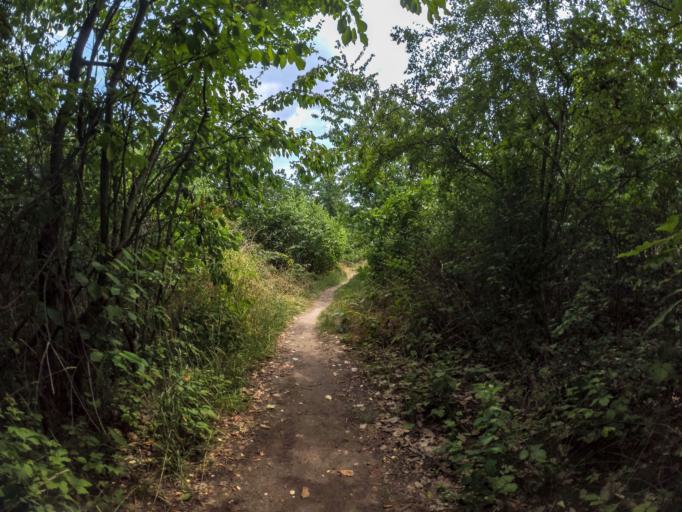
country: CZ
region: Central Bohemia
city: Neratovice
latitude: 50.2491
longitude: 14.5268
